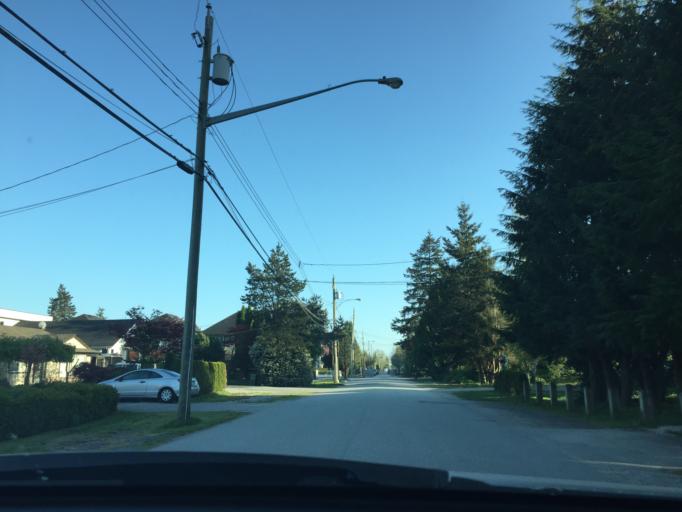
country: CA
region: British Columbia
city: Richmond
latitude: 49.1580
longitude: -123.1198
